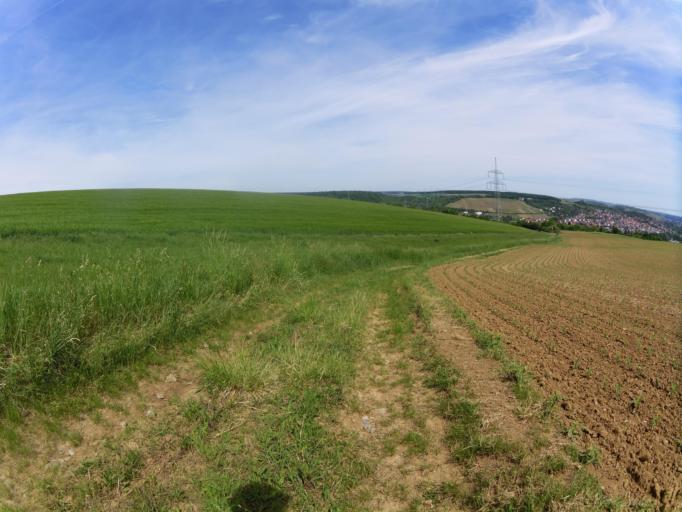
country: DE
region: Bavaria
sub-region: Regierungsbezirk Unterfranken
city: Ochsenfurt
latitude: 49.6682
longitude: 10.0309
